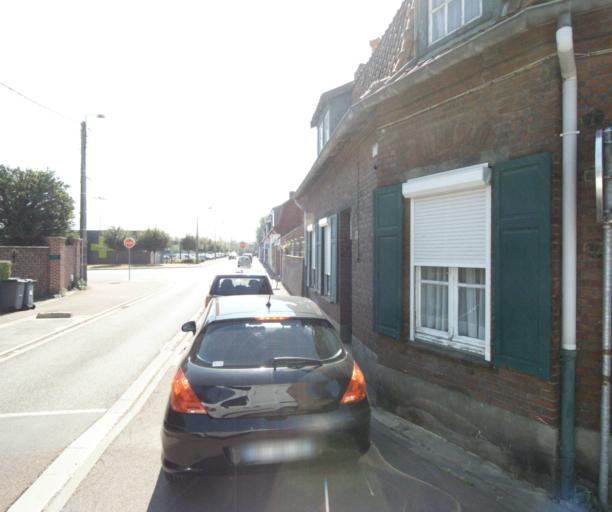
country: FR
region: Nord-Pas-de-Calais
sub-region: Departement du Nord
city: Bousbecque
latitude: 50.7709
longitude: 3.0816
